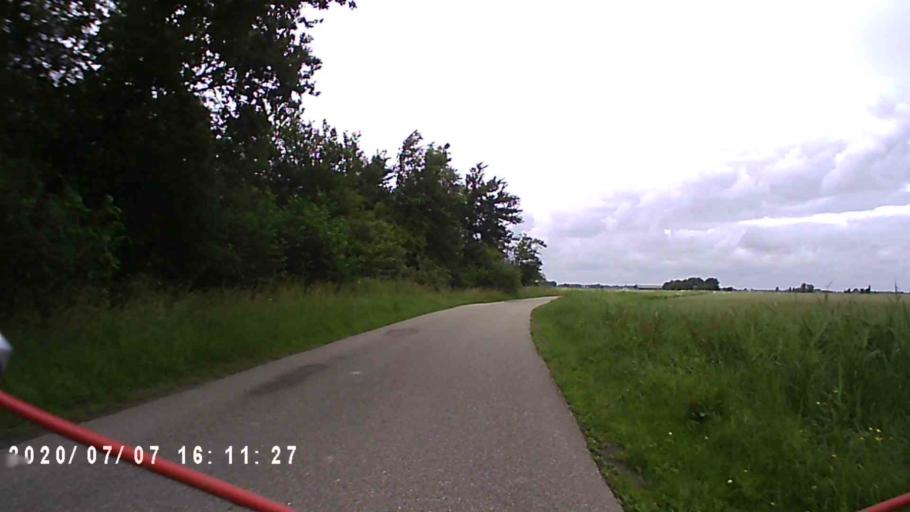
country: NL
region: Groningen
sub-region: Gemeente Winsum
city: Winsum
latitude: 53.3666
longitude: 6.5257
